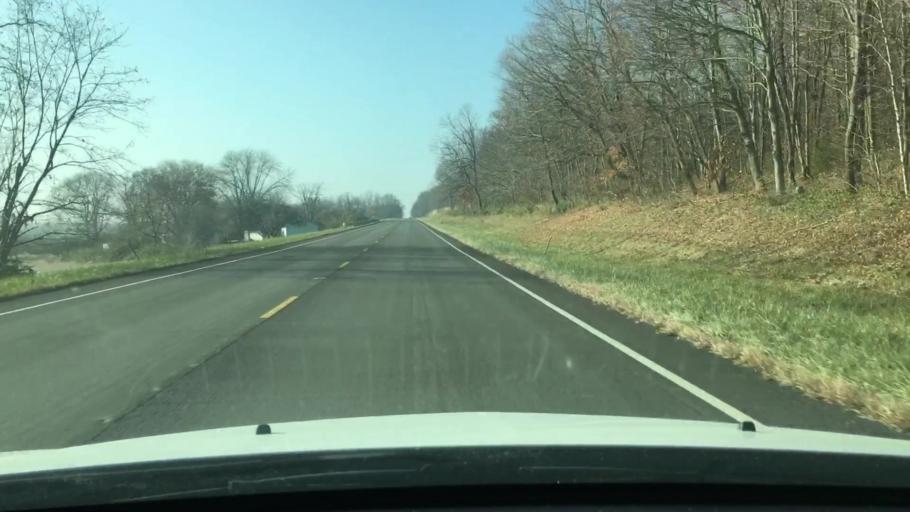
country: US
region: Illinois
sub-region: Peoria County
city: Glasford
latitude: 40.5116
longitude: -89.9196
